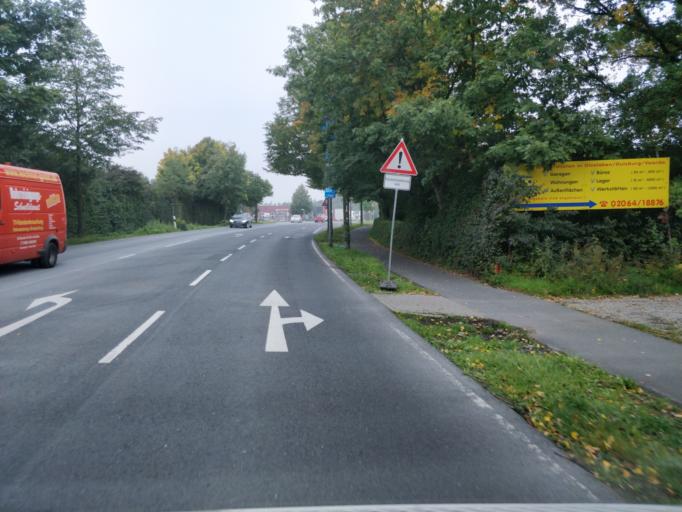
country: DE
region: North Rhine-Westphalia
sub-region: Regierungsbezirk Dusseldorf
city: Dinslaken
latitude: 51.5535
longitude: 6.7499
